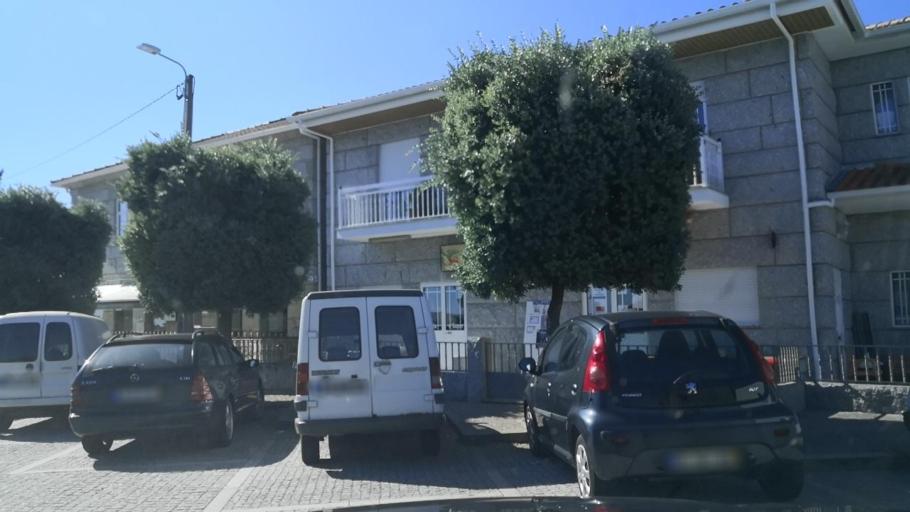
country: PT
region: Braga
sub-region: Fafe
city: Fafe
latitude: 41.4791
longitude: -8.1178
